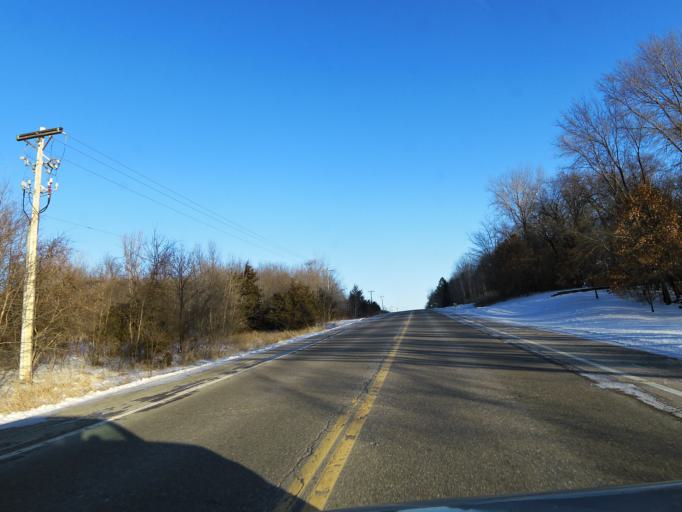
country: US
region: Minnesota
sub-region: Scott County
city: Elko New Market
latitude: 44.5439
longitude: -93.2281
